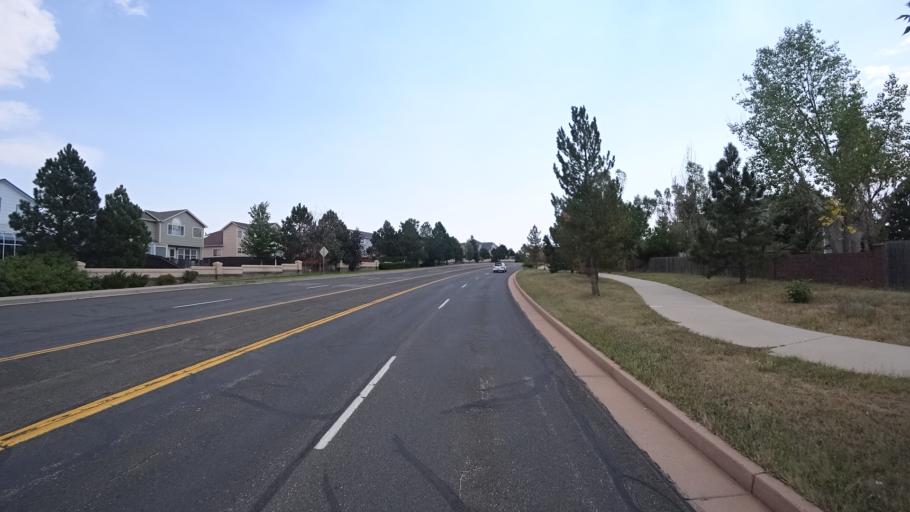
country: US
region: Colorado
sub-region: El Paso County
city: Black Forest
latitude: 38.9605
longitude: -104.7445
